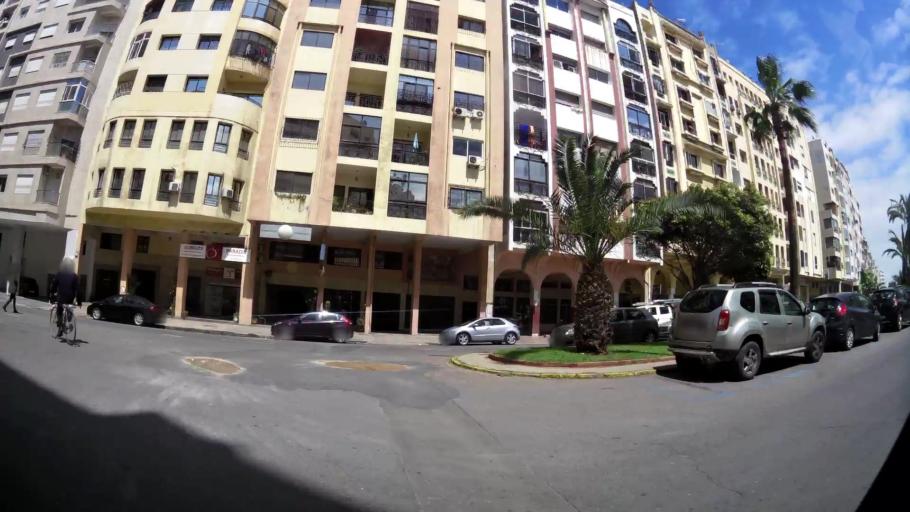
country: MA
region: Grand Casablanca
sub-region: Casablanca
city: Casablanca
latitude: 33.6000
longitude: -7.6375
